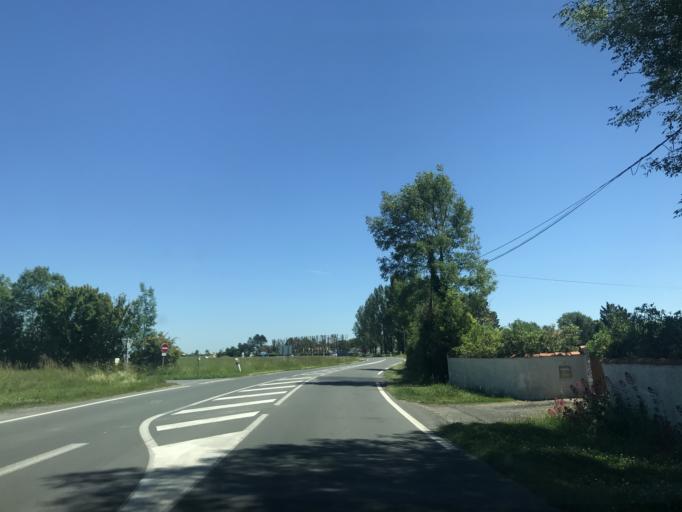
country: FR
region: Poitou-Charentes
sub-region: Departement de la Charente-Maritime
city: Meschers-sur-Gironde
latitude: 45.5627
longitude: -0.9455
